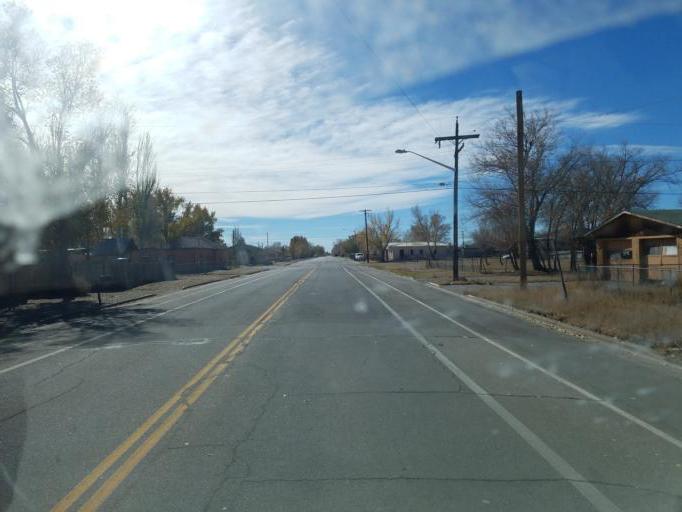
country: US
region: Colorado
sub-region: Alamosa County
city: Alamosa
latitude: 37.4621
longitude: -105.8702
